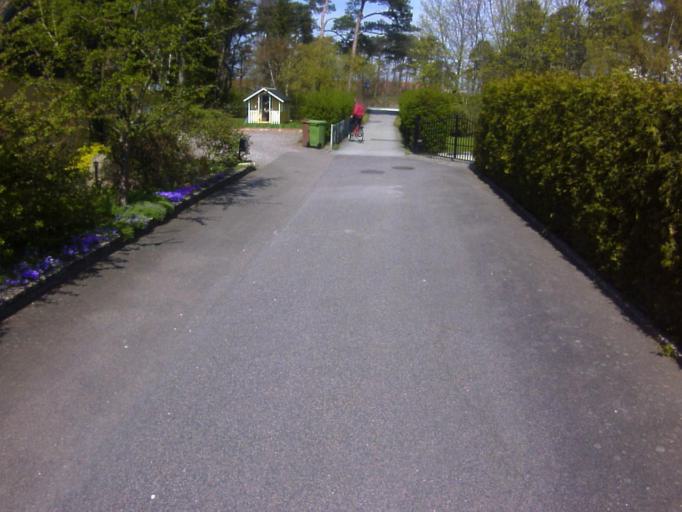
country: SE
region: Skane
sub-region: Kavlinge Kommun
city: Loddekopinge
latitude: 55.7654
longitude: 12.9945
